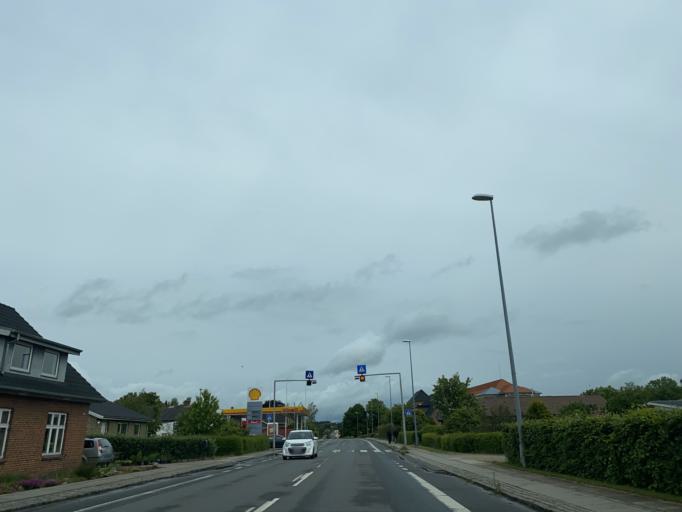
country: DK
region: Central Jutland
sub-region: Favrskov Kommune
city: Hammel
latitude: 56.2509
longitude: 9.8599
